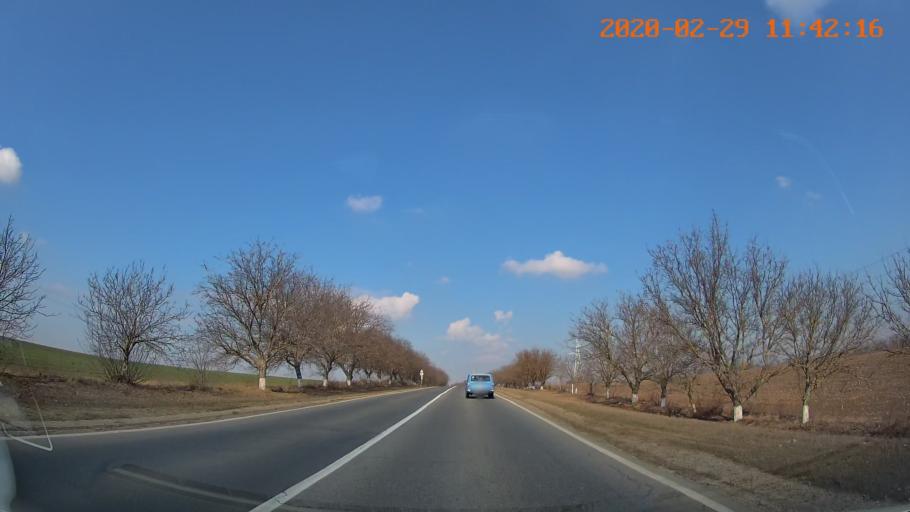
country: MD
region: Rezina
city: Saharna
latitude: 47.6816
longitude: 29.0135
